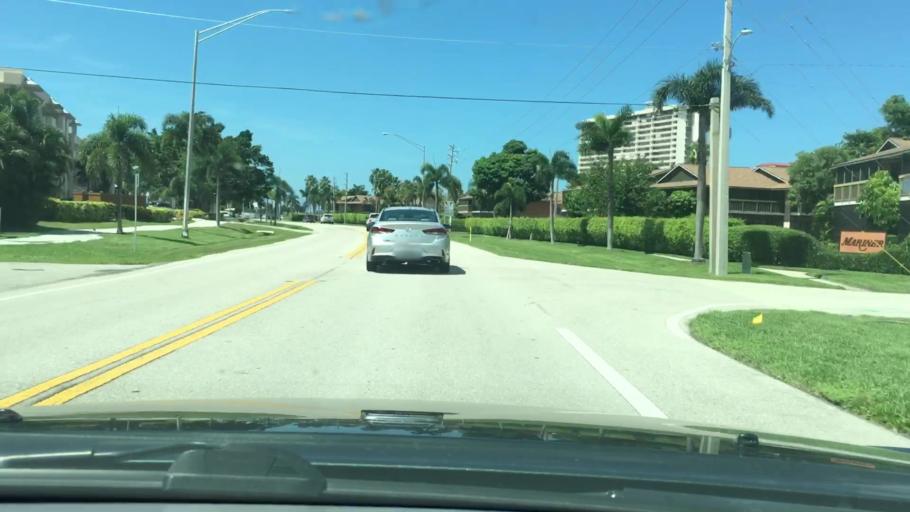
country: US
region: Florida
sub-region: Collier County
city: Marco
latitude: 25.9371
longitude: -81.7289
